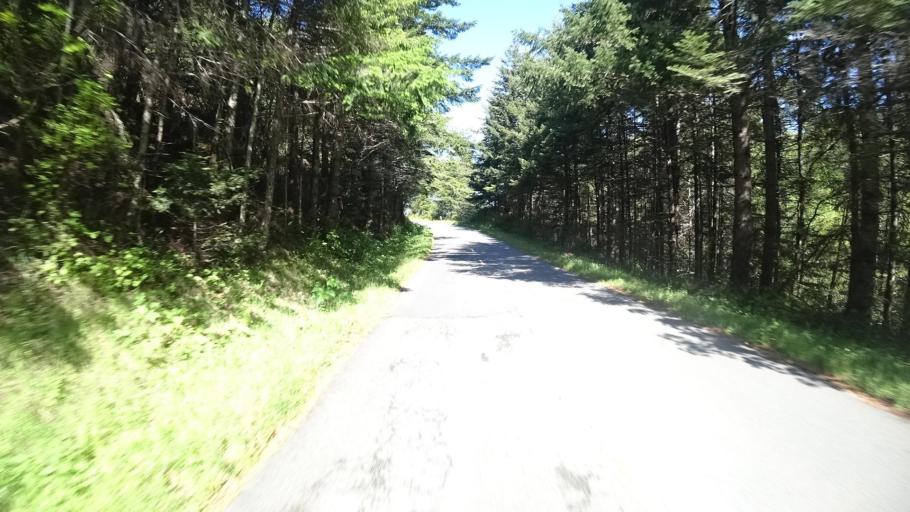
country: US
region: California
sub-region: Humboldt County
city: Ferndale
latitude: 40.3462
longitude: -124.3445
